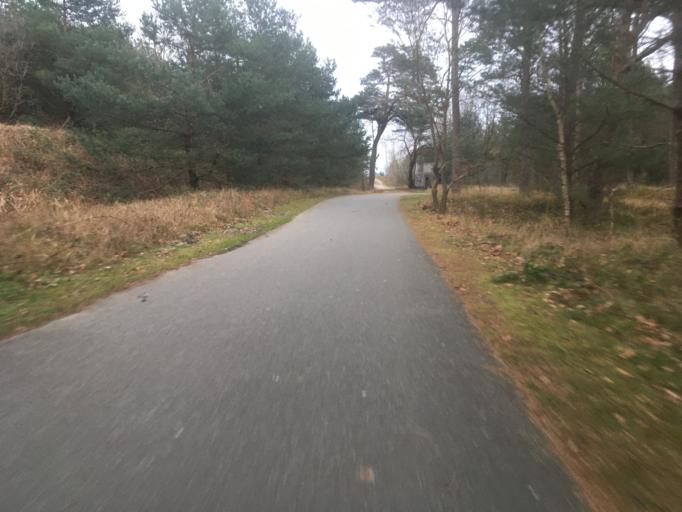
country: DE
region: Mecklenburg-Vorpommern
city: Sagard
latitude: 54.4716
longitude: 13.5678
